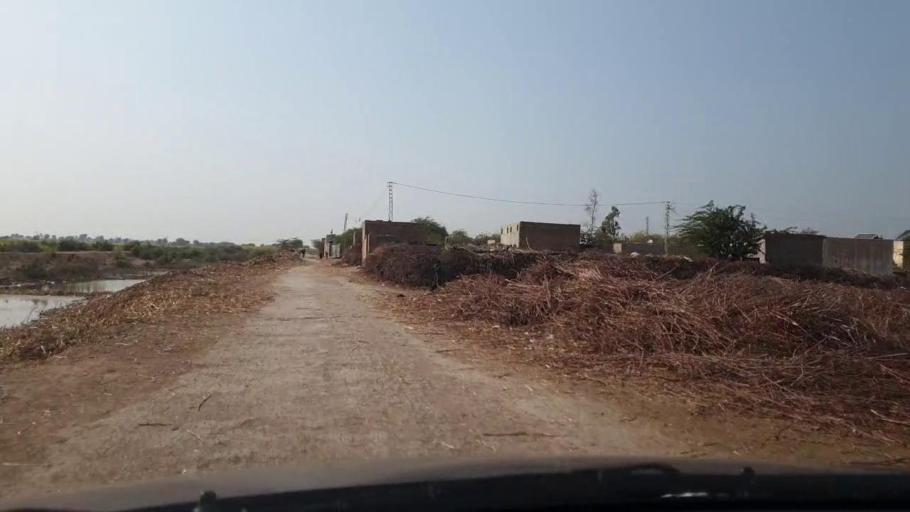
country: PK
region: Sindh
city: Sanghar
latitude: 26.0170
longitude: 68.9151
